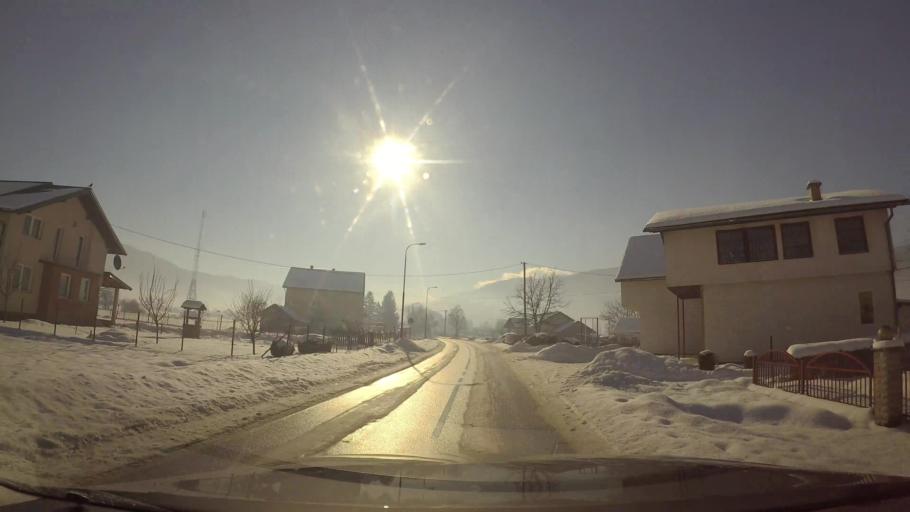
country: BA
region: Federation of Bosnia and Herzegovina
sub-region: Kanton Sarajevo
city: Sarajevo
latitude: 43.7956
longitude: 18.3520
